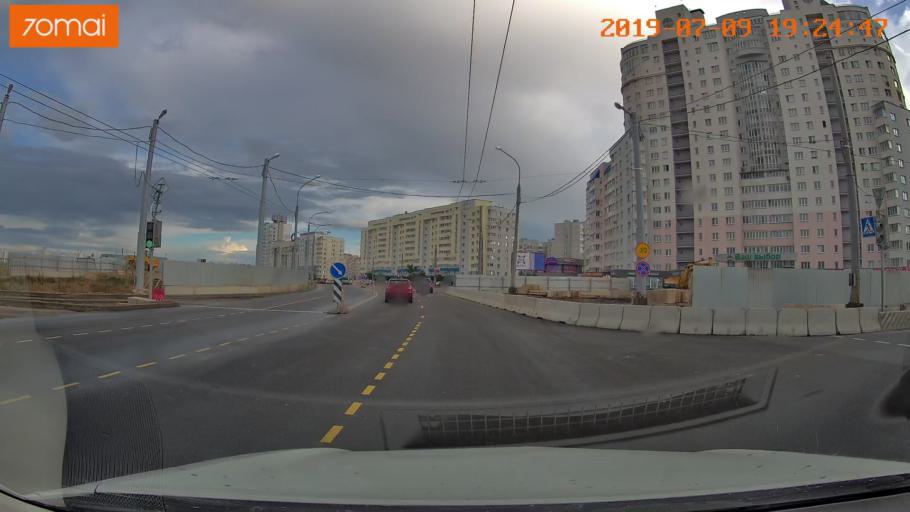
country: BY
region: Minsk
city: Syenitsa
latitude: 53.8461
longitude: 27.5693
